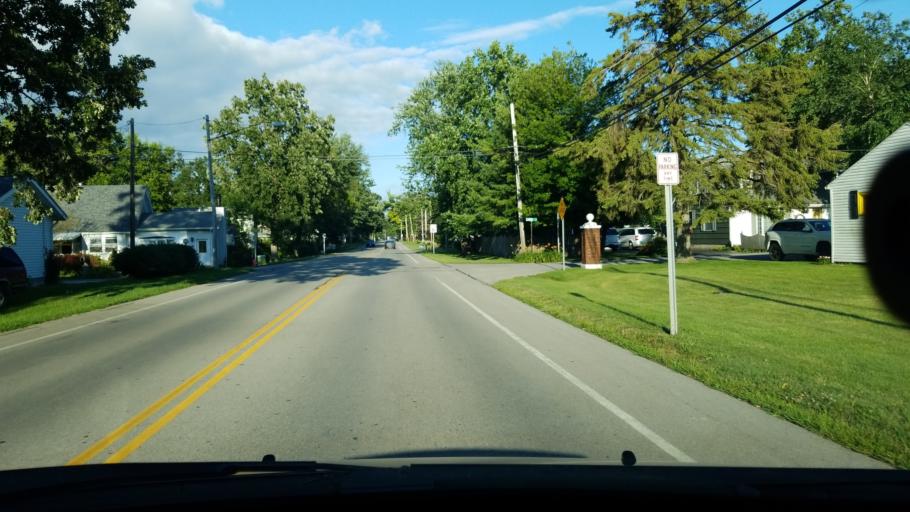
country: US
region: Ohio
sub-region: Erie County
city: Huron
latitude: 41.4083
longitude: -82.5842
